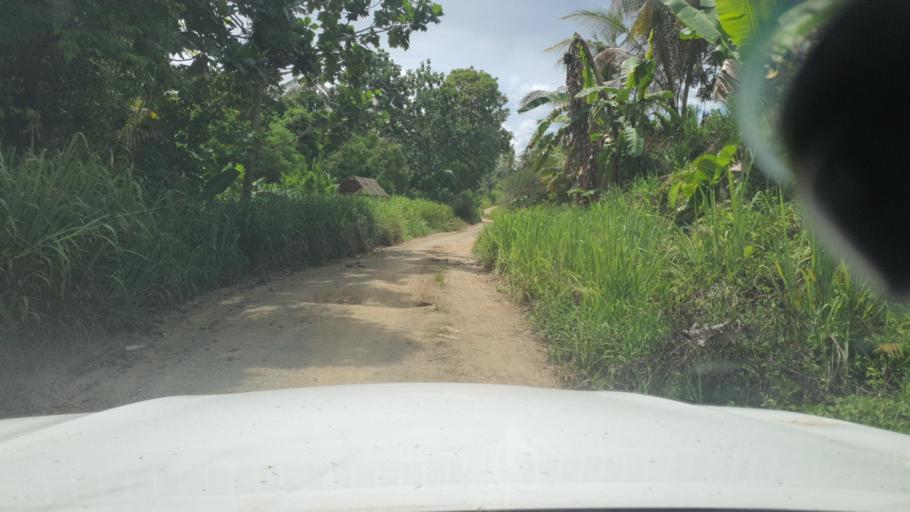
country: SB
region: Guadalcanal
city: Honiara
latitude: -9.4843
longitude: 160.3382
